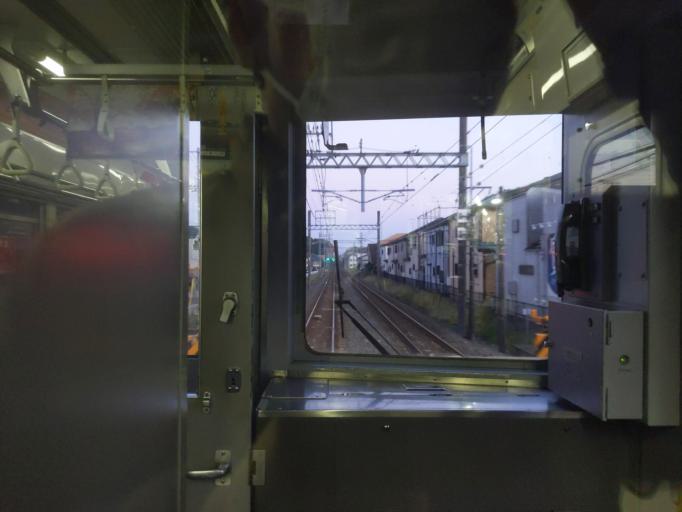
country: JP
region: Chiba
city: Nagareyama
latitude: 35.8706
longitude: 139.9293
